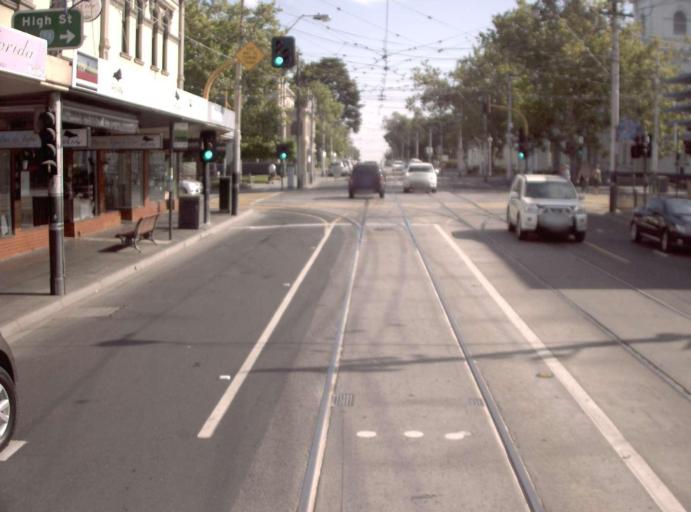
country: AU
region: Victoria
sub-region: Glen Eira
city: Caulfield North
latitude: -37.8571
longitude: 145.0292
